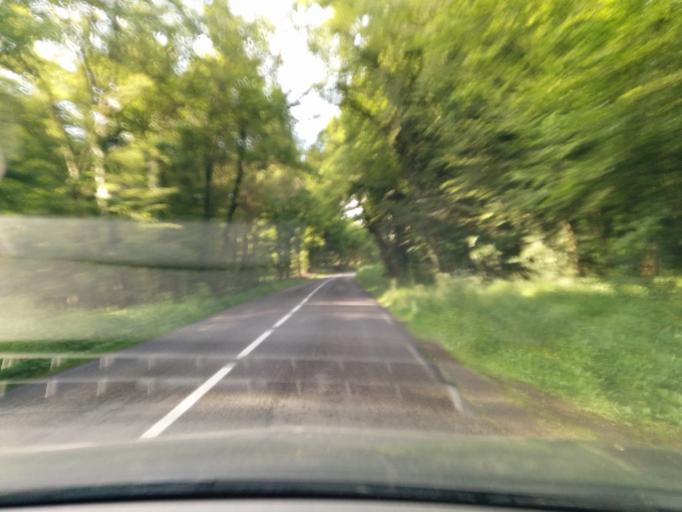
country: FR
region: Haute-Normandie
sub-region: Departement de l'Eure
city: Courcelles-sur-Seine
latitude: 49.1771
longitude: 1.3881
